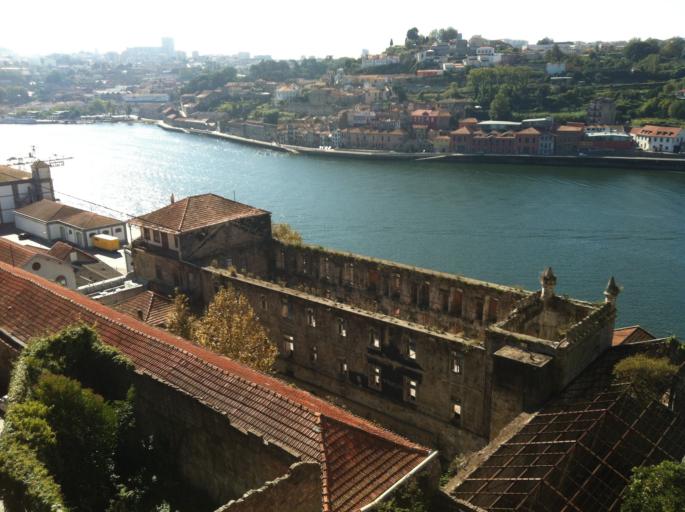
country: PT
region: Porto
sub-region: Vila Nova de Gaia
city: Vila Nova de Gaia
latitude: 41.1454
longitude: -8.6242
